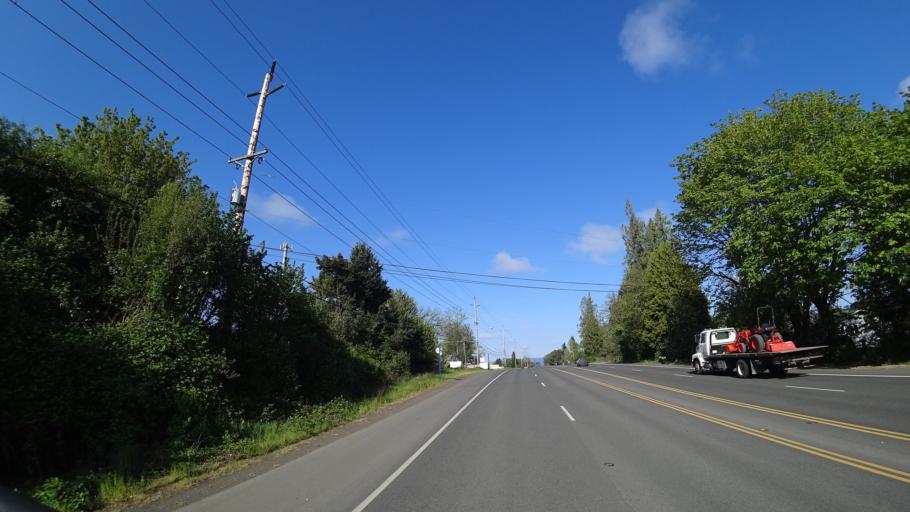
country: US
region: Oregon
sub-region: Washington County
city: Hillsboro
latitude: 45.5199
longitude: -123.0171
